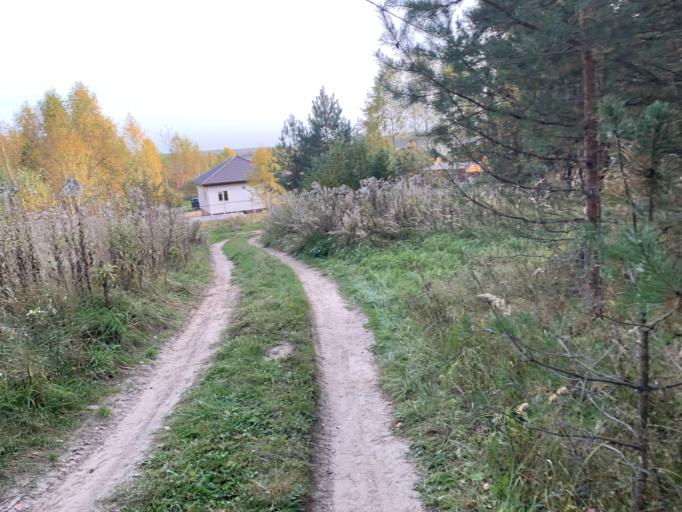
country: RU
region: Jaroslavl
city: Petrovsk
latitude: 56.9821
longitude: 39.3755
